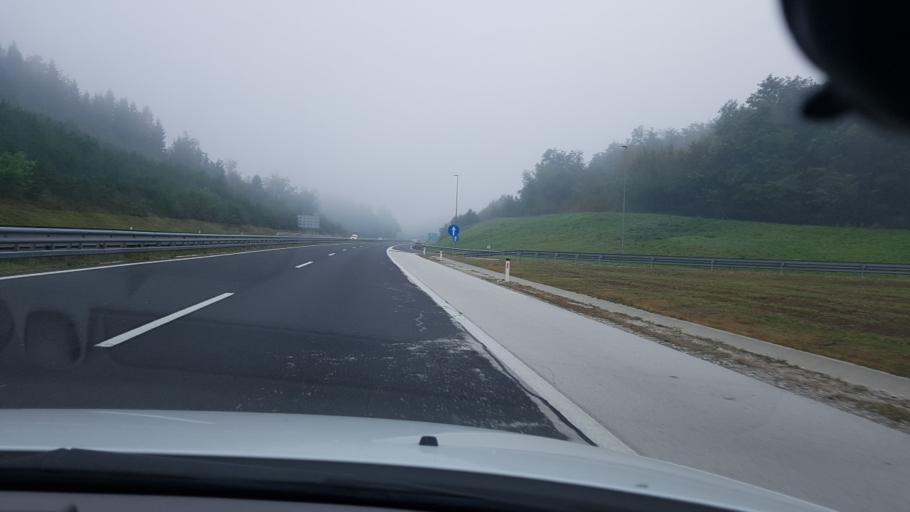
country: SI
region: Novo Mesto
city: Novo Mesto
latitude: 45.8309
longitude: 15.1774
